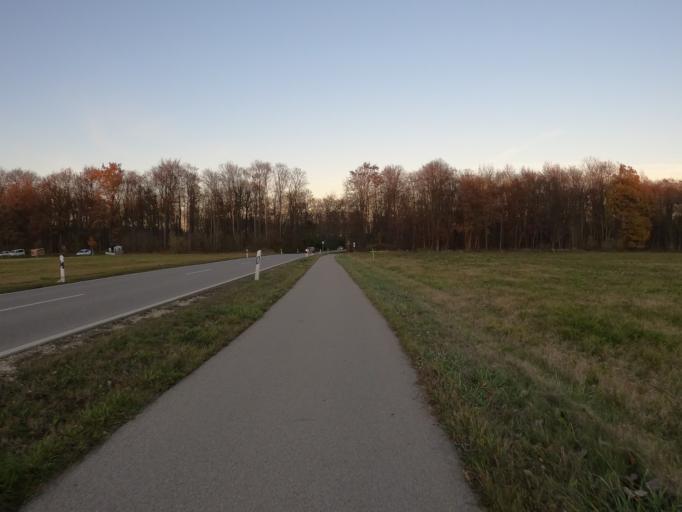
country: DE
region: Bavaria
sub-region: Swabia
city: Nersingen
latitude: 48.4298
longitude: 10.0855
